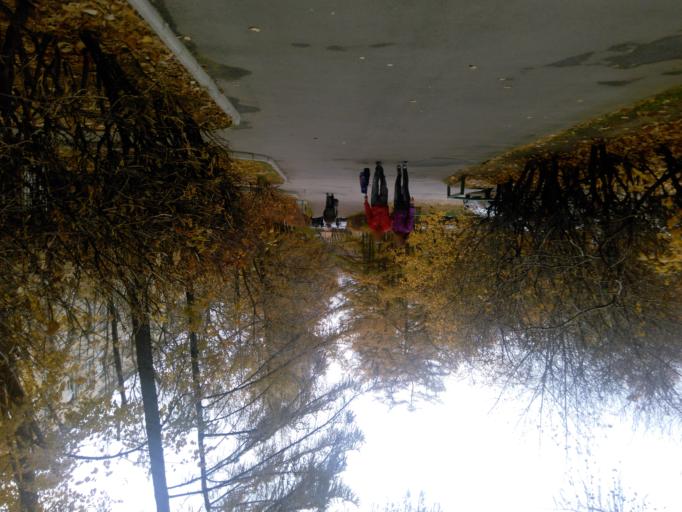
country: RU
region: Moscow
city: Mar'ina Roshcha
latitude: 55.8045
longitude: 37.6435
